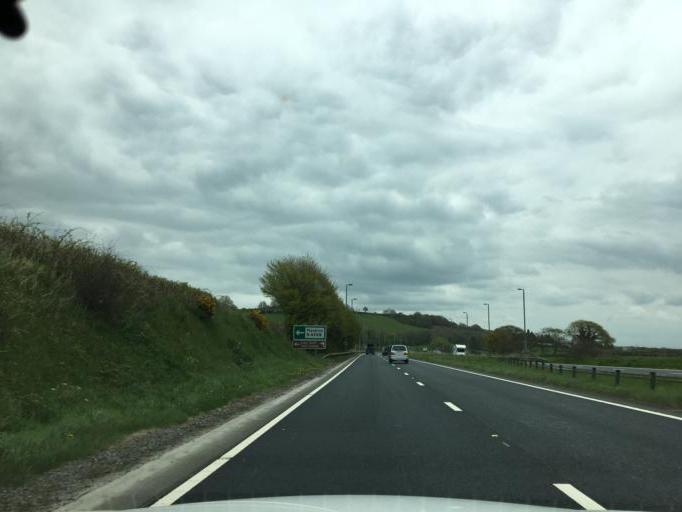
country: GB
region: Wales
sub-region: Carmarthenshire
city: Llangynog
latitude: 51.8461
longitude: -4.3957
